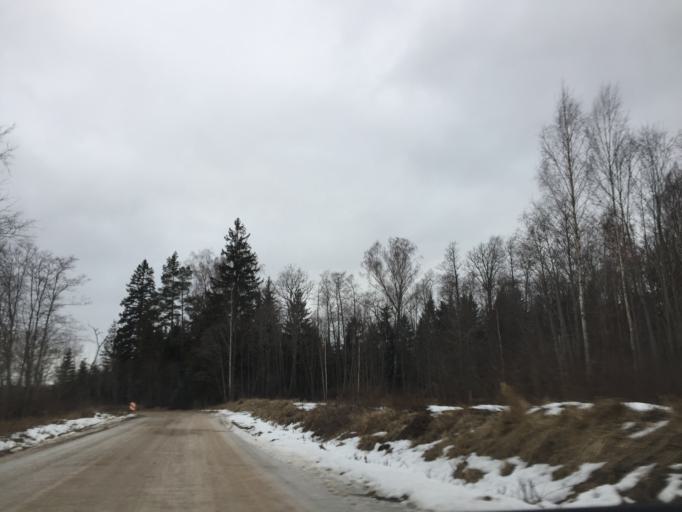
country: LV
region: Salacgrivas
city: Salacgriva
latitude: 57.6482
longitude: 24.4158
